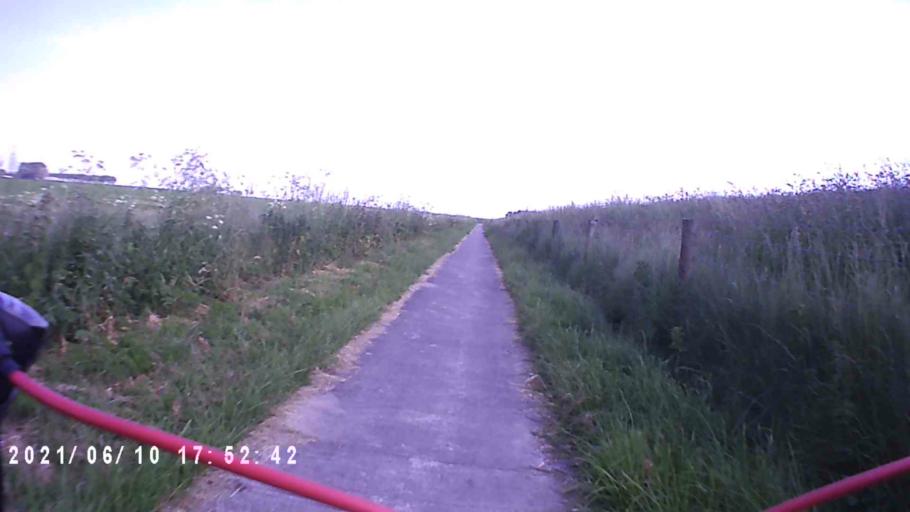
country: NL
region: Groningen
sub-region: Gemeente De Marne
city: Ulrum
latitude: 53.3278
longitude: 6.3192
